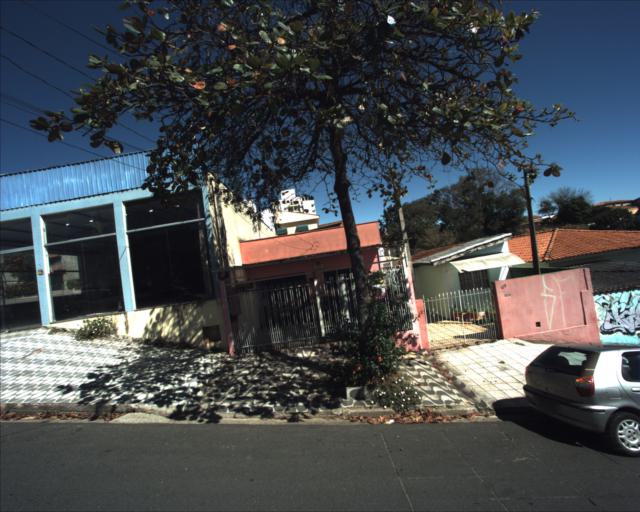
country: BR
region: Sao Paulo
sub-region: Sorocaba
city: Sorocaba
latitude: -23.5058
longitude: -47.4902
